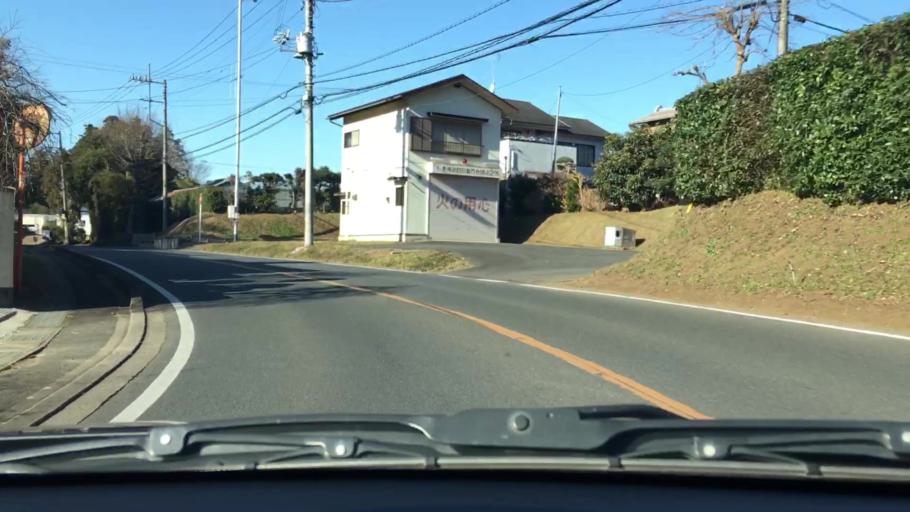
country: JP
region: Chiba
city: Shisui
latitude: 35.7000
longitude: 140.2534
